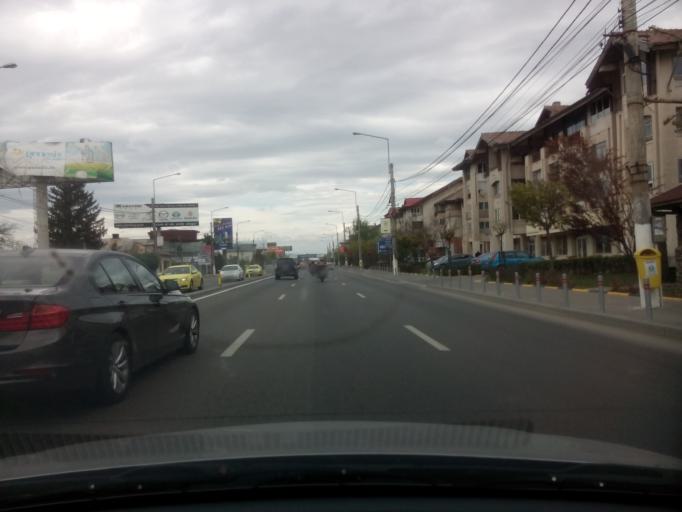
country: RO
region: Ilfov
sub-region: Comuna Otopeni
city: Otopeni
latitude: 44.5475
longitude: 26.0689
